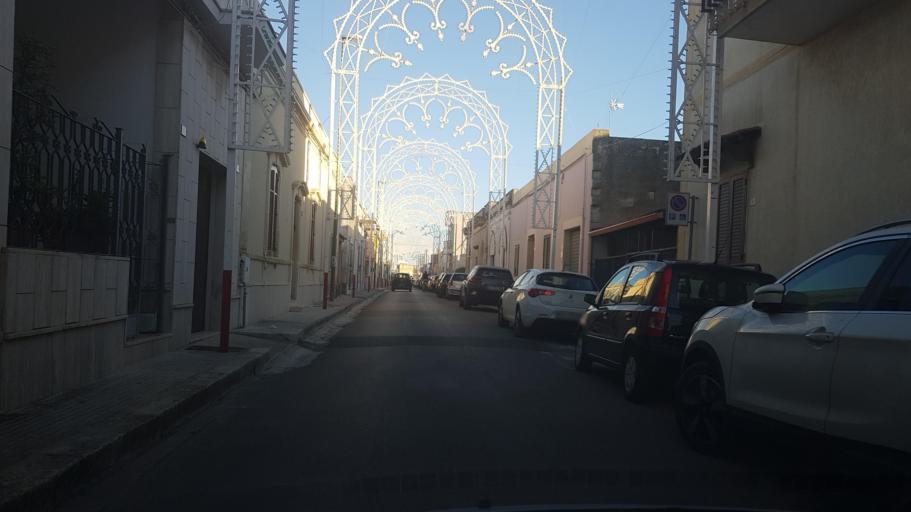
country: IT
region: Apulia
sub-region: Provincia di Lecce
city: Struda
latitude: 40.3201
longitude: 18.2821
